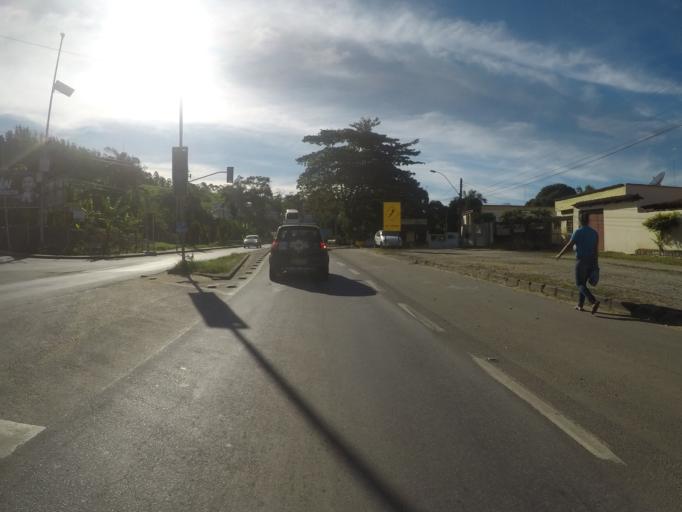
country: BR
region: Espirito Santo
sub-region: Fundao
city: Fundao
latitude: -19.9316
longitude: -40.4055
